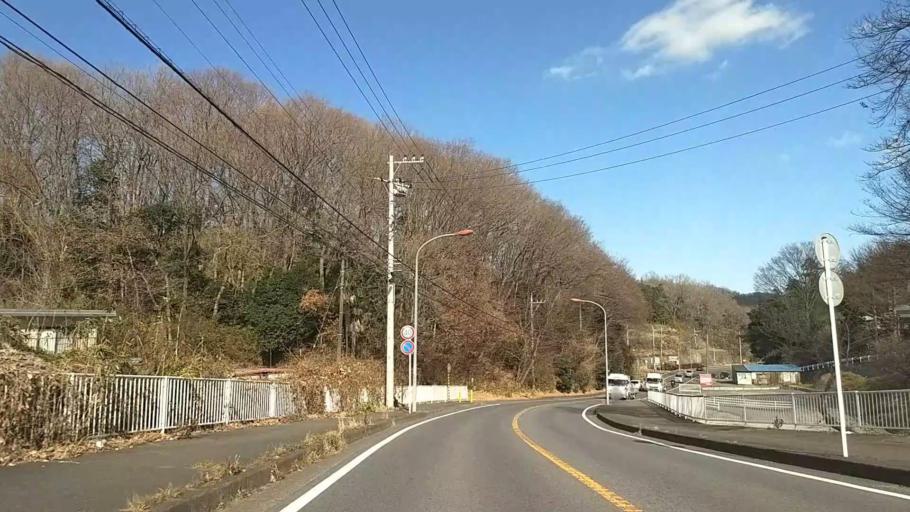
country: JP
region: Kanagawa
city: Isehara
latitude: 35.4284
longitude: 139.3053
